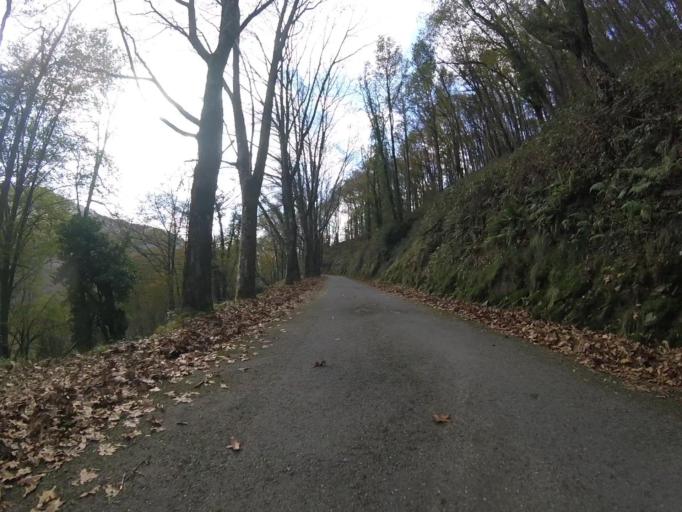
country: ES
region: Navarre
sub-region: Provincia de Navarra
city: Goizueta
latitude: 43.2150
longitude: -1.8049
